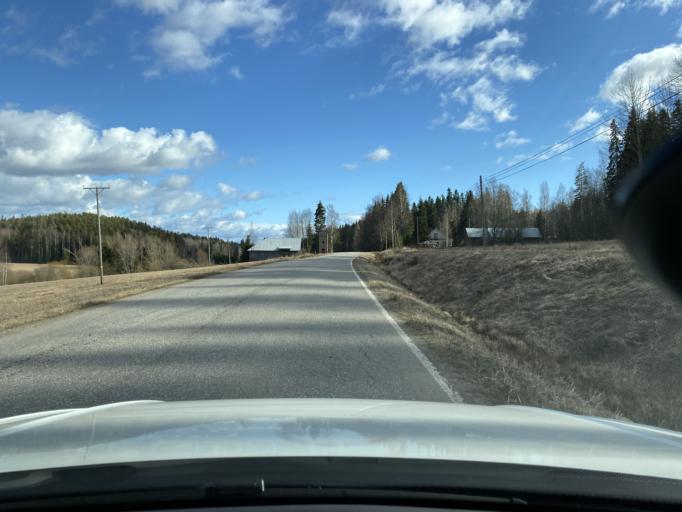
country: FI
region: Pirkanmaa
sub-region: Lounais-Pirkanmaa
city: Punkalaidun
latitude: 61.0803
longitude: 23.1642
